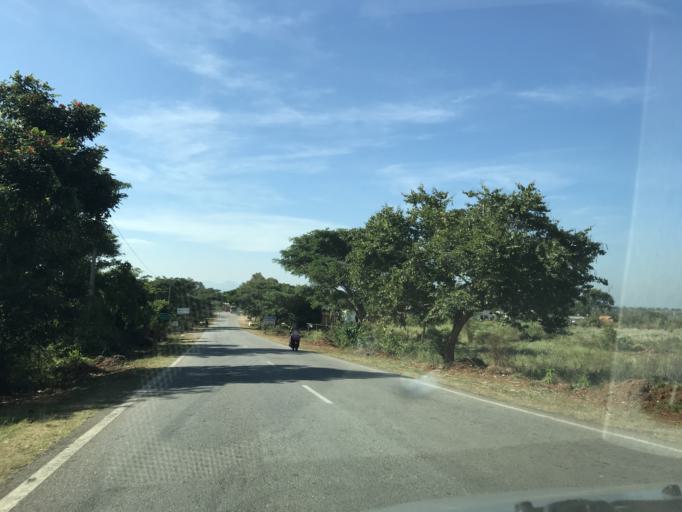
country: IN
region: Karnataka
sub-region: Mysore
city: Nanjangud
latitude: 12.1351
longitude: 76.5081
